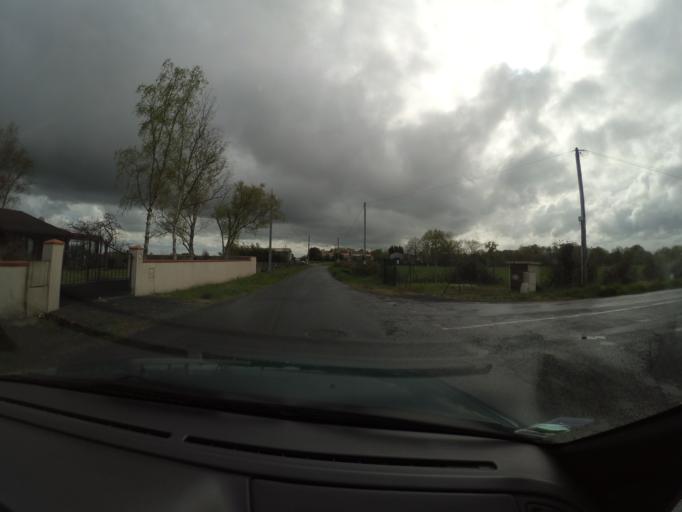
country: FR
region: Pays de la Loire
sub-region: Departement de la Loire-Atlantique
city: Maisdon-sur-Sevre
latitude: 47.0959
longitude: -1.3658
